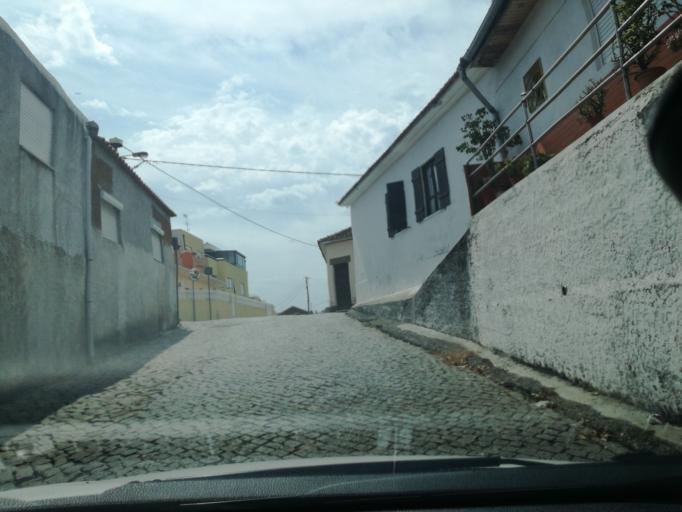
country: PT
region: Porto
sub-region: Vila Nova de Gaia
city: Grijo
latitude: 41.0190
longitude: -8.5855
